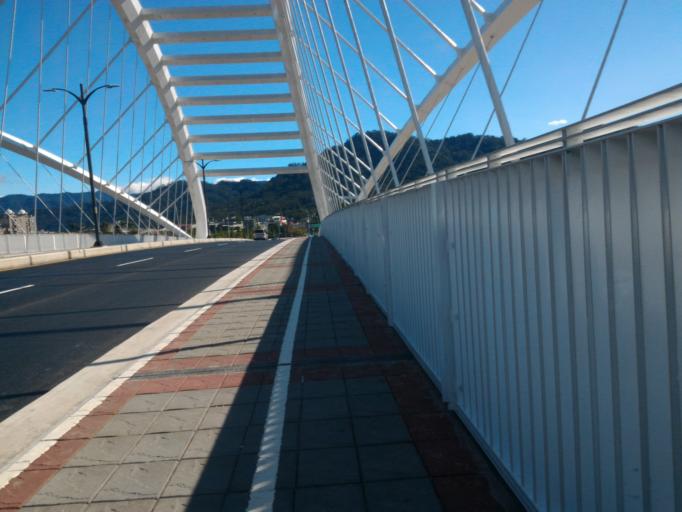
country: TW
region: Taiwan
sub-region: Taoyuan
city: Taoyuan
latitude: 24.9375
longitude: 121.3884
